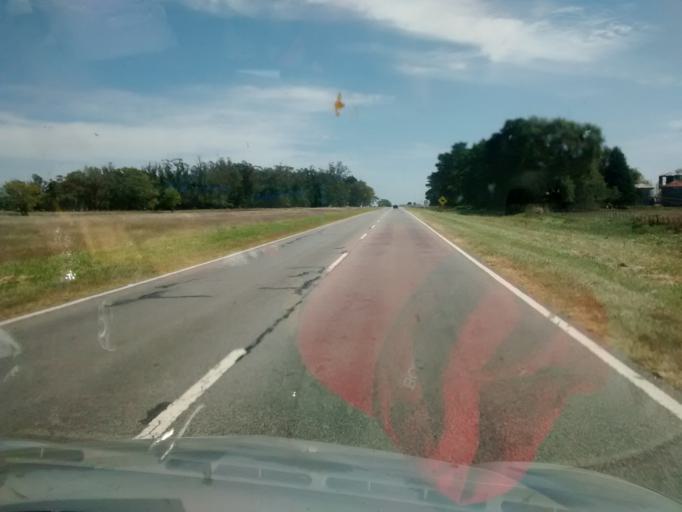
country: AR
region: Buenos Aires
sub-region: Partido de Balcarce
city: Balcarce
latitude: -37.6693
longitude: -58.5332
